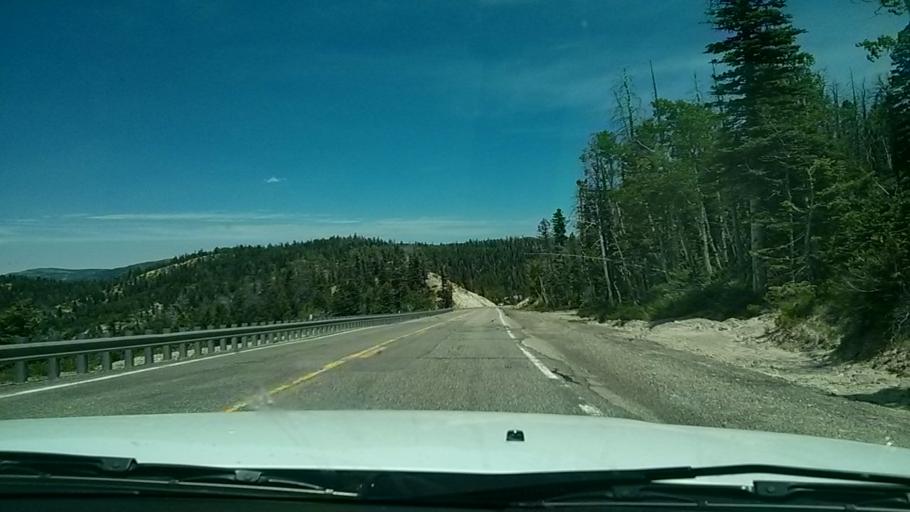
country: US
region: Utah
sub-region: Iron County
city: Cedar City
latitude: 37.5830
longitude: -112.8835
